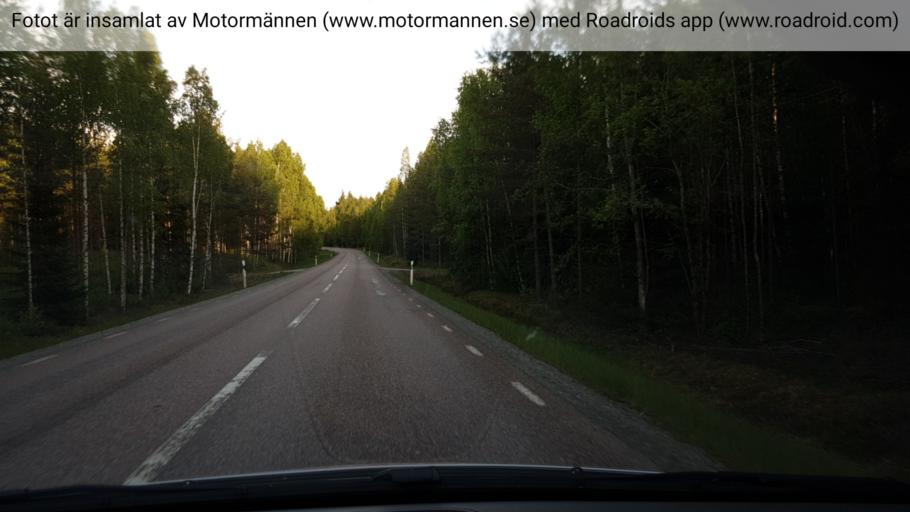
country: SE
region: Vaestmanland
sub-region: Fagersta Kommun
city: Fagersta
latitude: 59.9397
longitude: 15.8084
